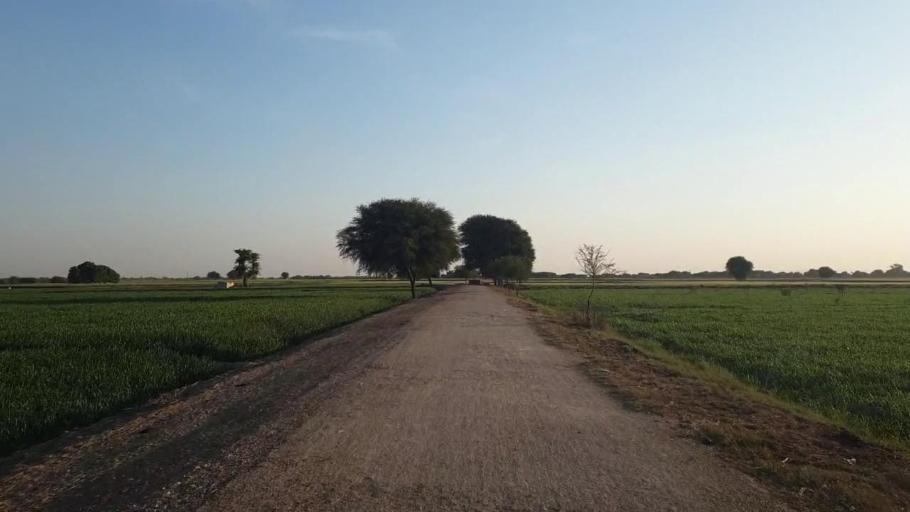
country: PK
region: Sindh
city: Chambar
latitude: 25.2694
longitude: 68.7656
